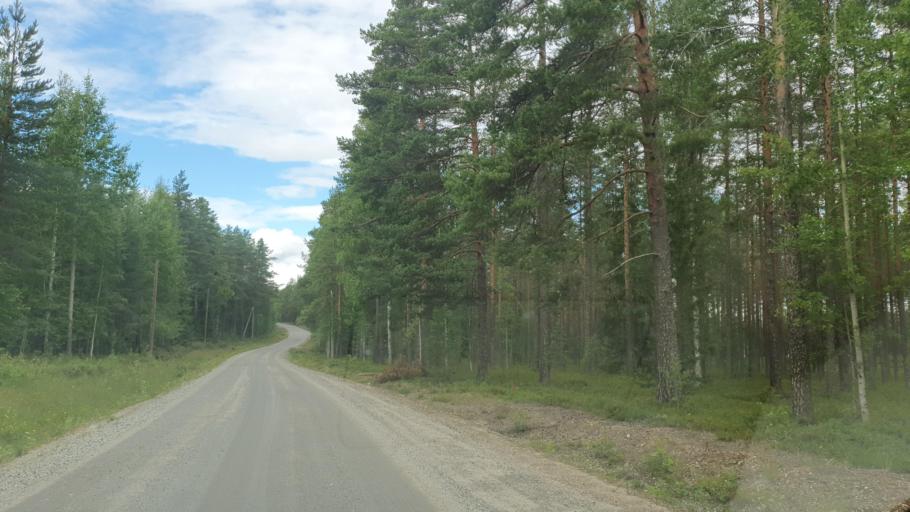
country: FI
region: Kainuu
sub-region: Kehys-Kainuu
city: Kuhmo
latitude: 64.1050
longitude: 29.3980
